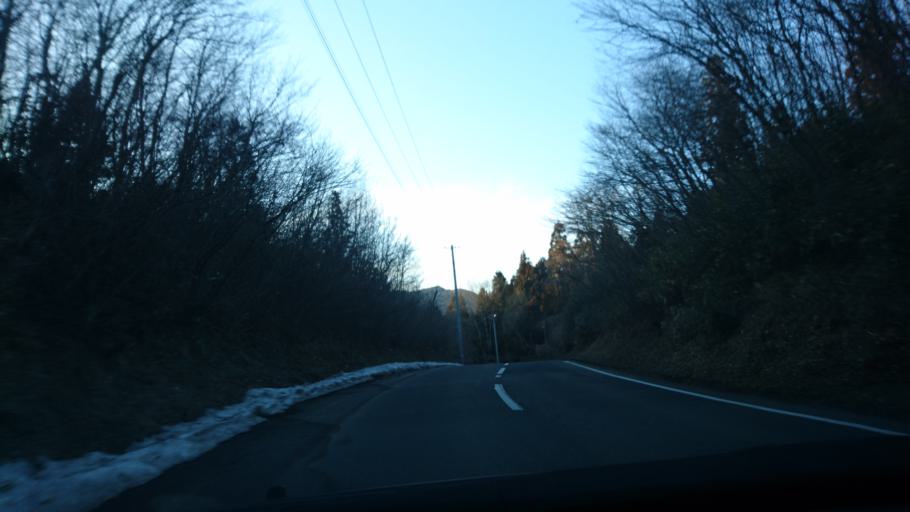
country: JP
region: Iwate
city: Mizusawa
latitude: 39.0451
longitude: 141.3361
